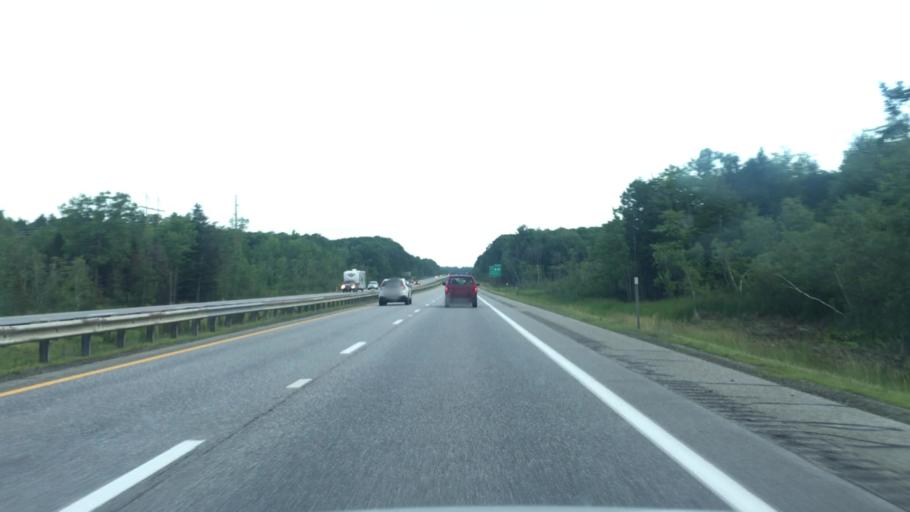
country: US
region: Maine
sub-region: Kennebec County
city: Hallowell
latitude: 44.2557
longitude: -69.8073
